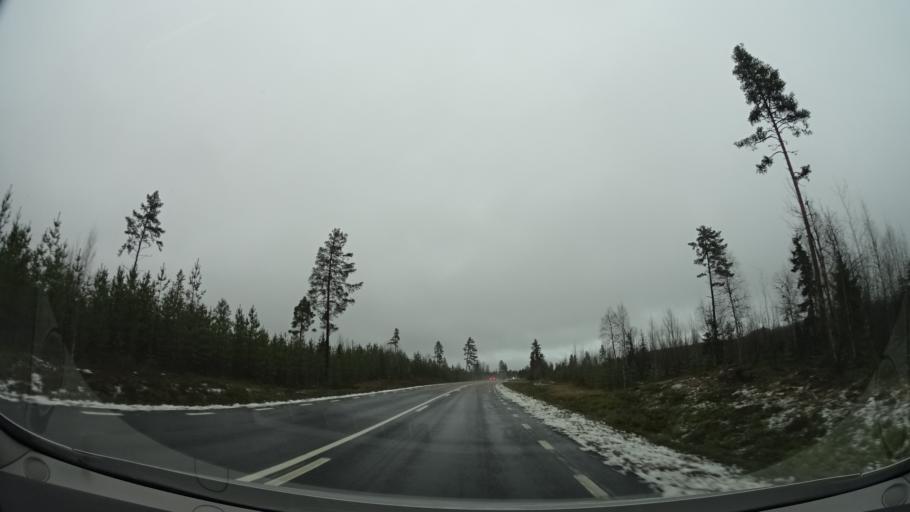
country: SE
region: Vaesterbotten
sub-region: Dorotea Kommun
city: Dorotea
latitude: 64.2138
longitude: 16.2871
